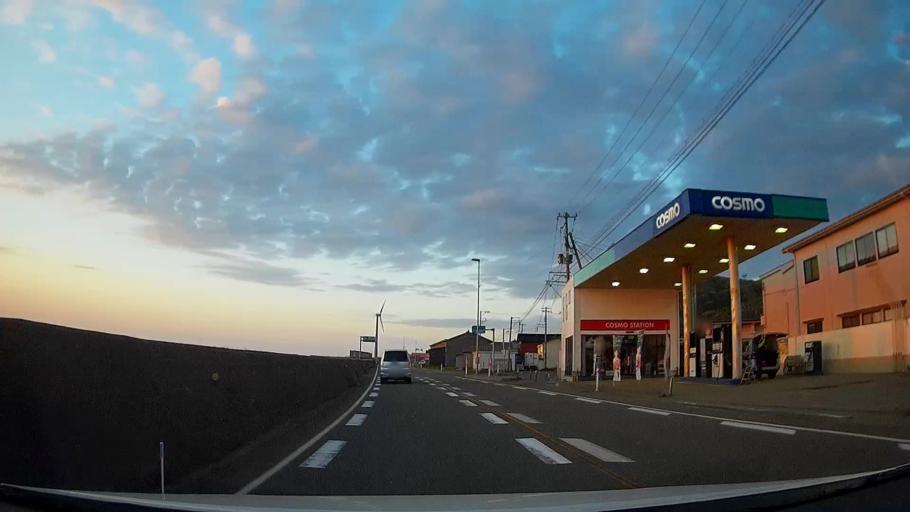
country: JP
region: Niigata
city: Joetsu
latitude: 37.1576
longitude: 138.0833
